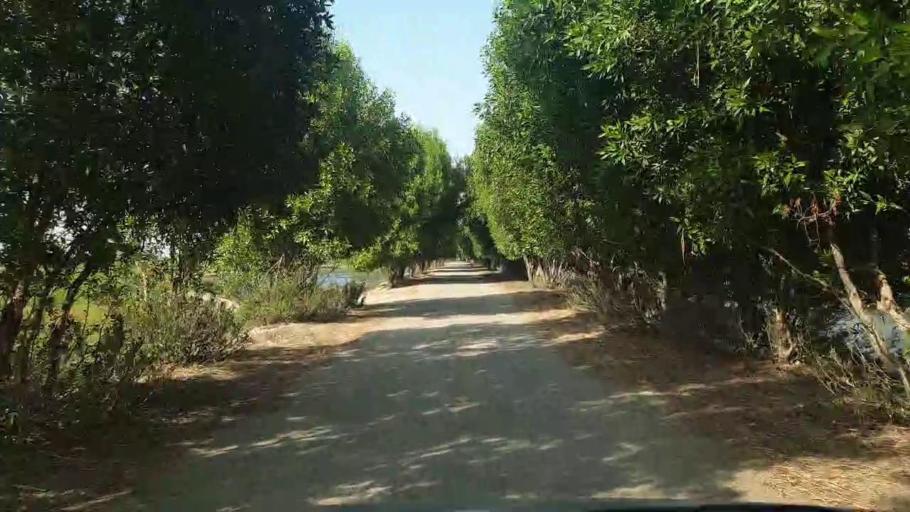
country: PK
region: Sindh
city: Badin
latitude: 24.6228
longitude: 68.8148
